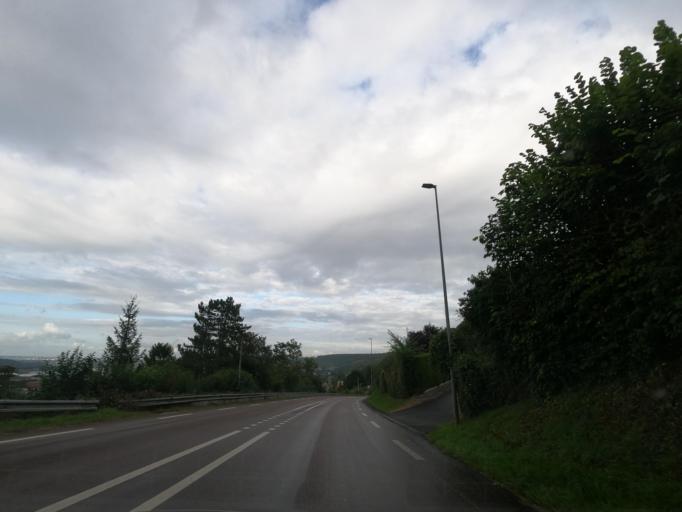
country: FR
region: Haute-Normandie
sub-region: Departement de la Seine-Maritime
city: Sahurs
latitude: 49.3408
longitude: 0.9589
